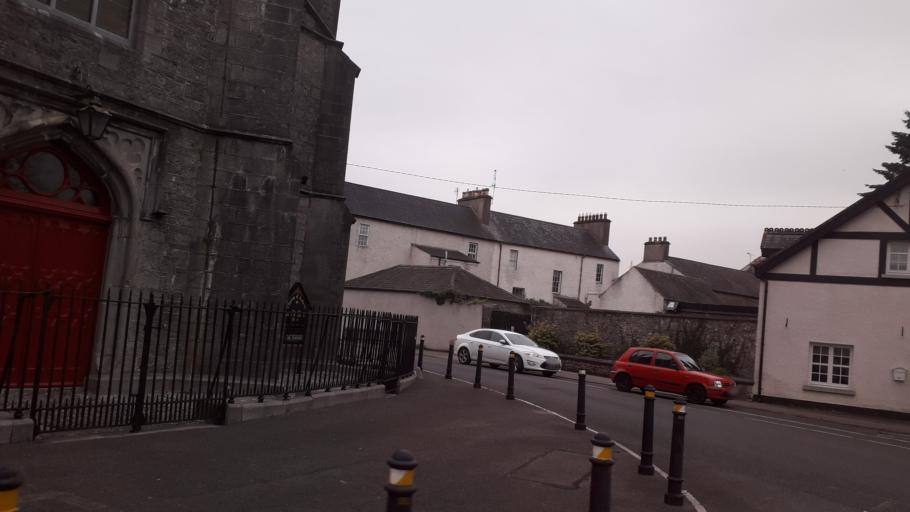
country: IE
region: Leinster
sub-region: Uibh Fhaili
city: Birr
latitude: 53.0982
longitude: -7.9105
